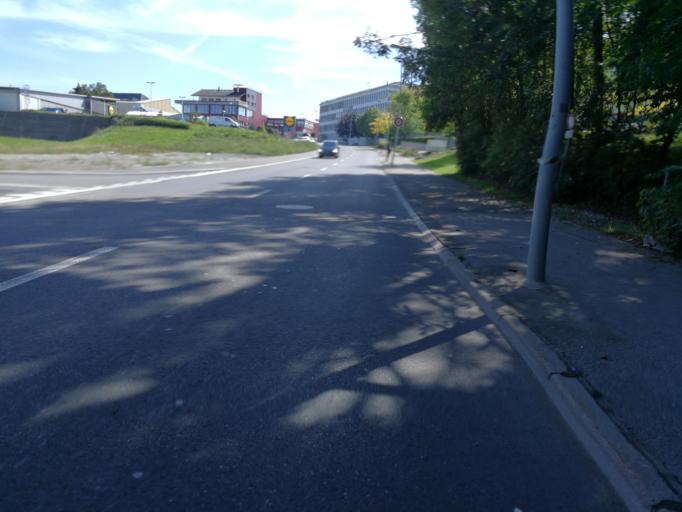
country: CH
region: Zurich
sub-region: Bezirk Horgen
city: Au / Unter-Dorf
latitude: 47.2375
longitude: 8.6344
